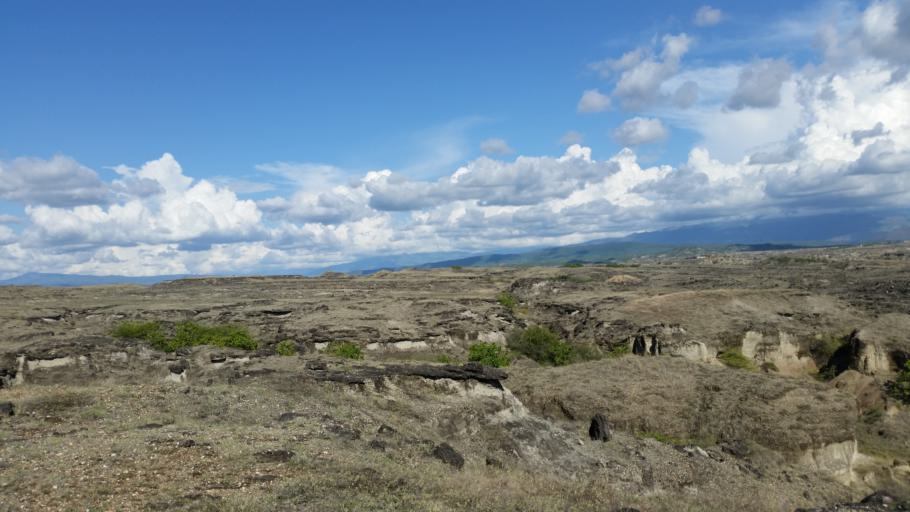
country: CO
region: Huila
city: Villavieja
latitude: 3.2521
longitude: -75.1451
